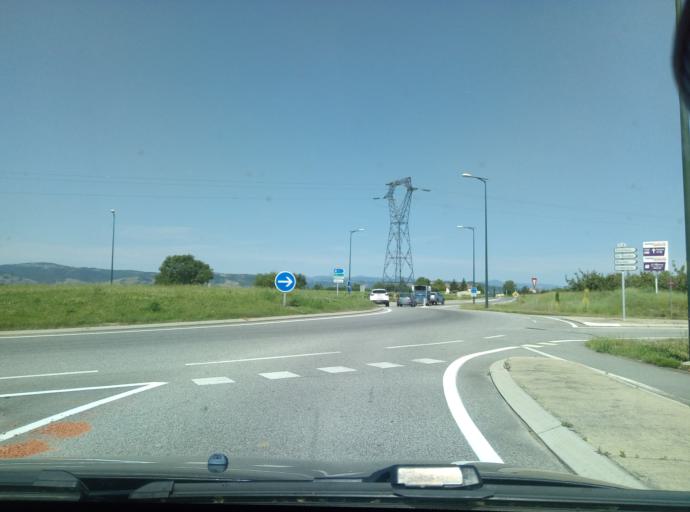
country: FR
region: Rhone-Alpes
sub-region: Departement de la Drome
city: Chanos-Curson
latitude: 45.0604
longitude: 4.9070
